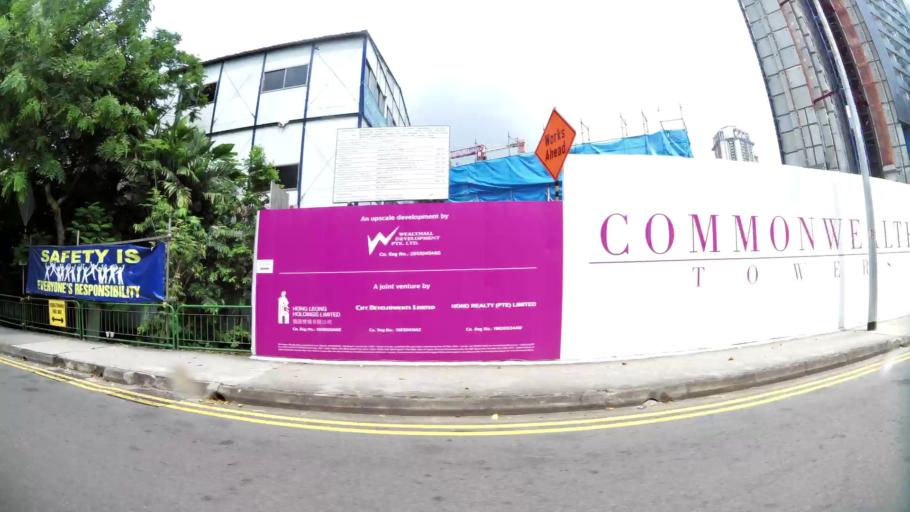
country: SG
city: Singapore
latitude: 1.2961
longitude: 103.8054
